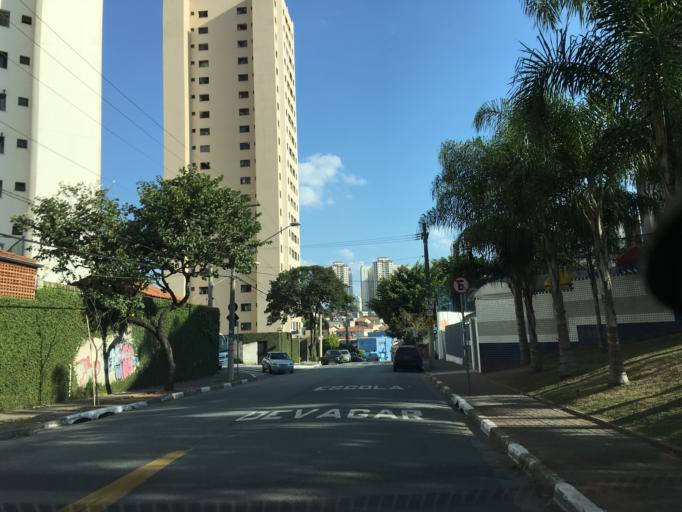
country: BR
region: Sao Paulo
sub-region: Sao Paulo
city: Sao Paulo
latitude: -23.4715
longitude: -46.6344
